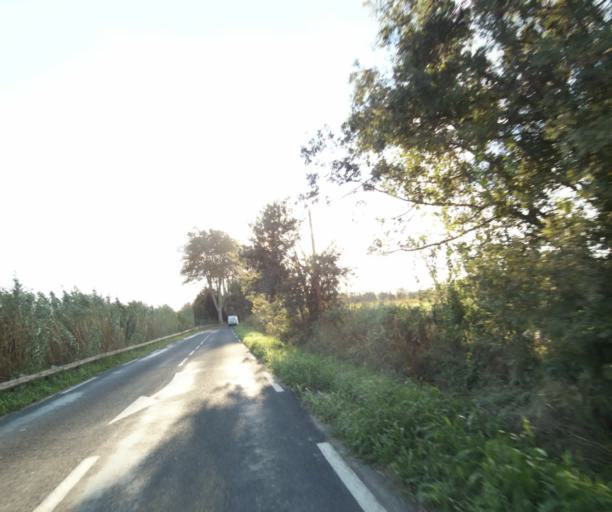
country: FR
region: Languedoc-Roussillon
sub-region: Departement des Pyrenees-Orientales
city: Elne
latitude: 42.5831
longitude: 2.9829
